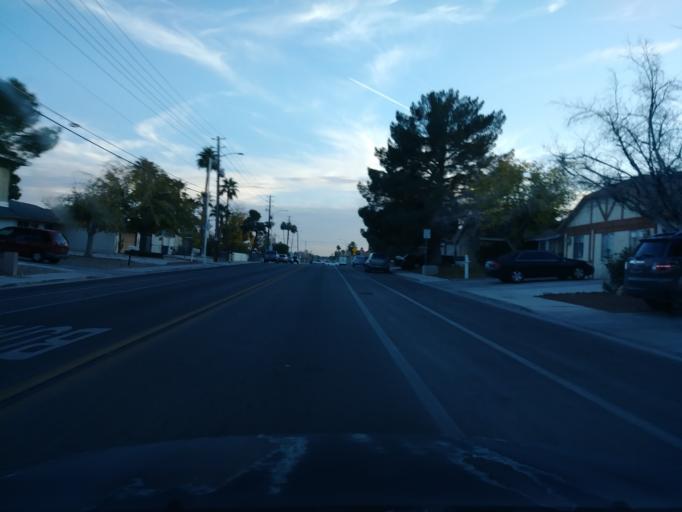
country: US
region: Nevada
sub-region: Clark County
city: Spring Valley
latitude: 36.1681
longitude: -115.2422
